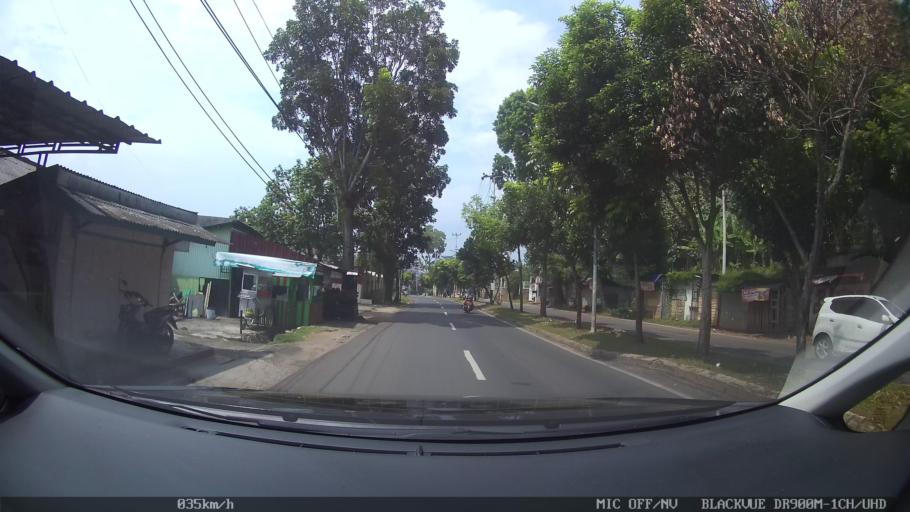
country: ID
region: Lampung
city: Bandarlampung
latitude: -5.4234
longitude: 105.2477
